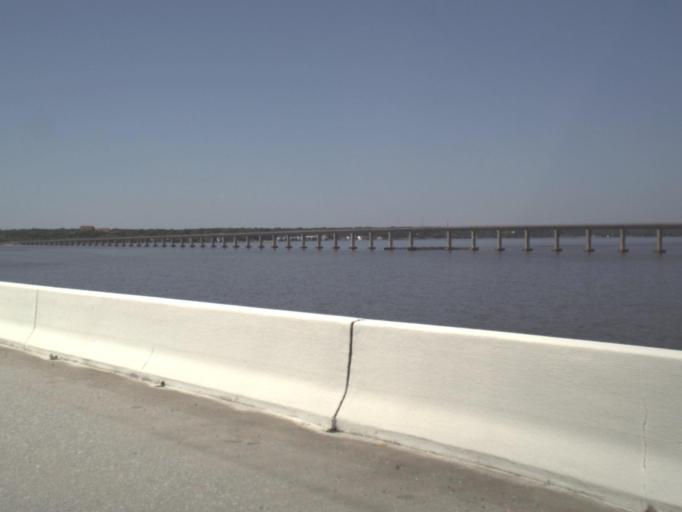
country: US
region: Florida
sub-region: Escambia County
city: Ferry Pass
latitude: 30.5211
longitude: -87.1415
